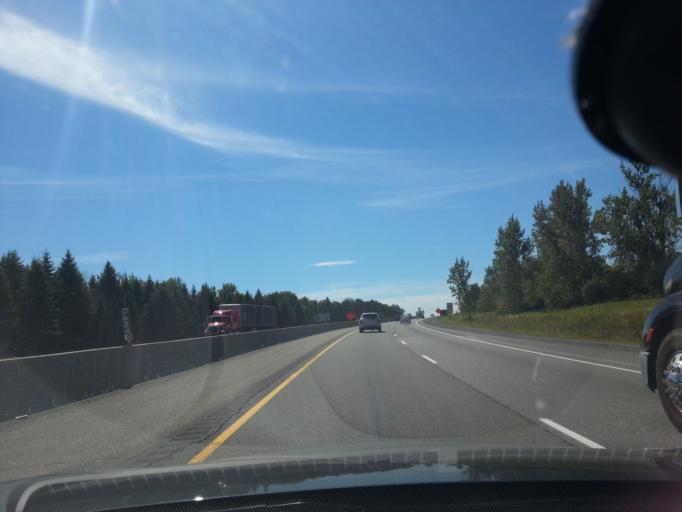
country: CA
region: Ontario
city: Kingston
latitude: 44.2950
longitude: -76.4181
